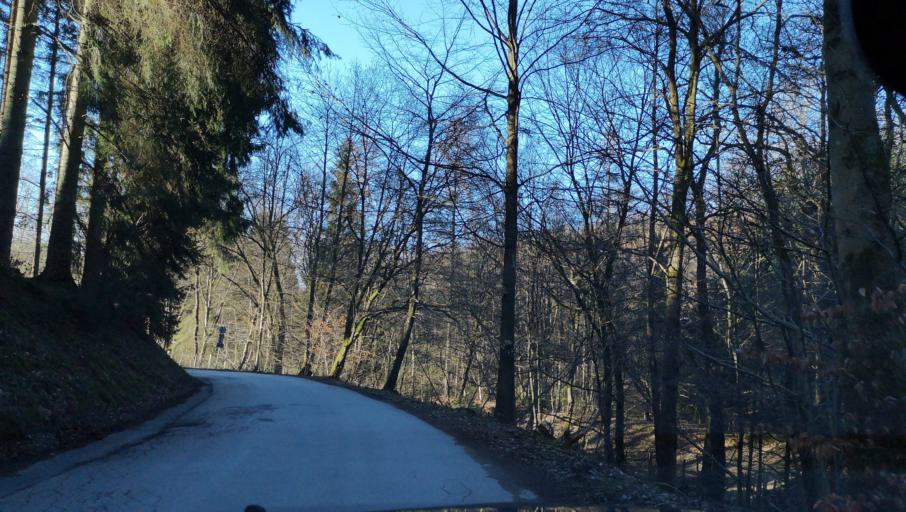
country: DE
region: North Rhine-Westphalia
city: Ennepetal
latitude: 51.2591
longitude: 7.3711
